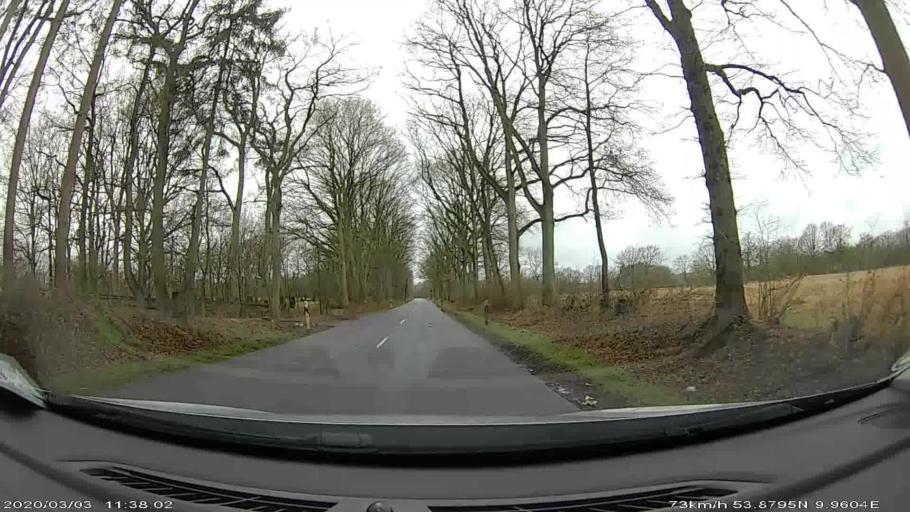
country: DE
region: Schleswig-Holstein
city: Schmalfeld
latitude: 53.8798
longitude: 9.9555
